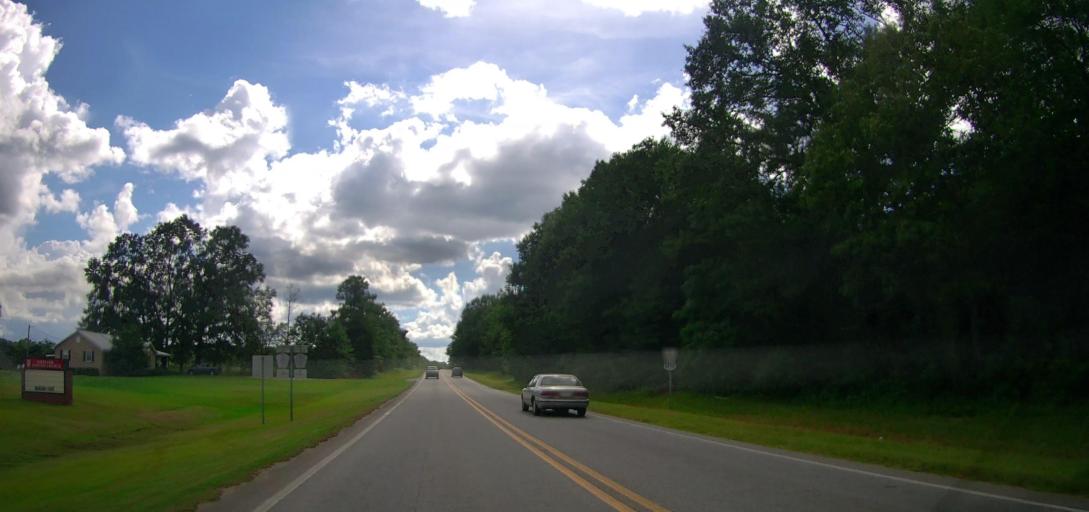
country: US
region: Alabama
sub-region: Russell County
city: Ladonia
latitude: 32.4429
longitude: -85.2924
